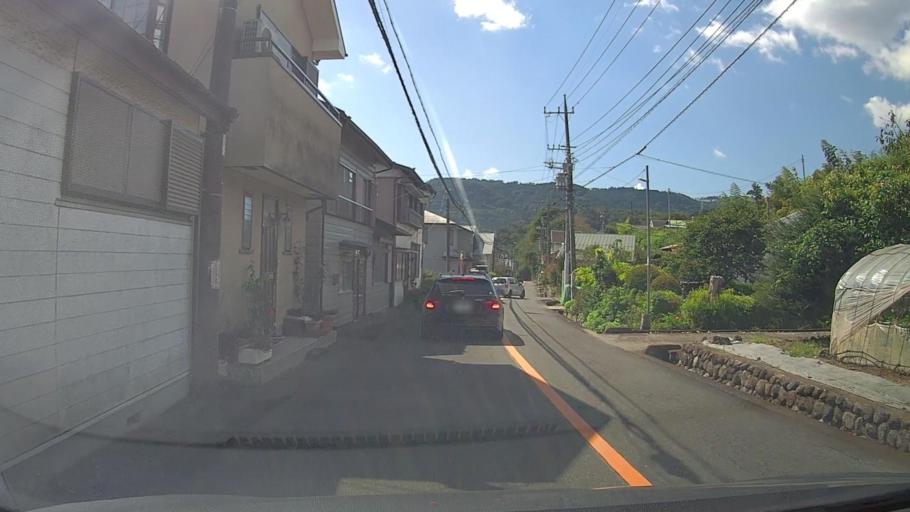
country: JP
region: Kanagawa
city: Hadano
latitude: 35.3754
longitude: 139.1688
